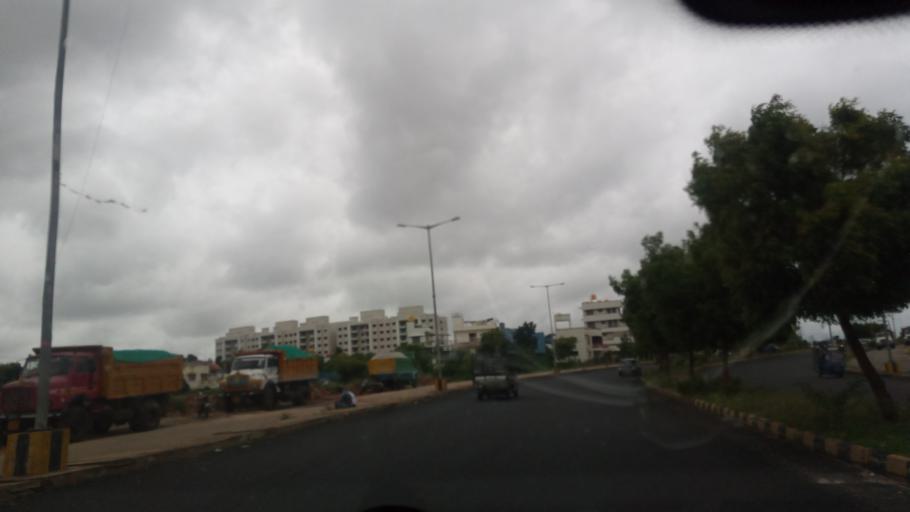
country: IN
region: Karnataka
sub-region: Mysore
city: Mysore
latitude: 12.3129
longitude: 76.5959
